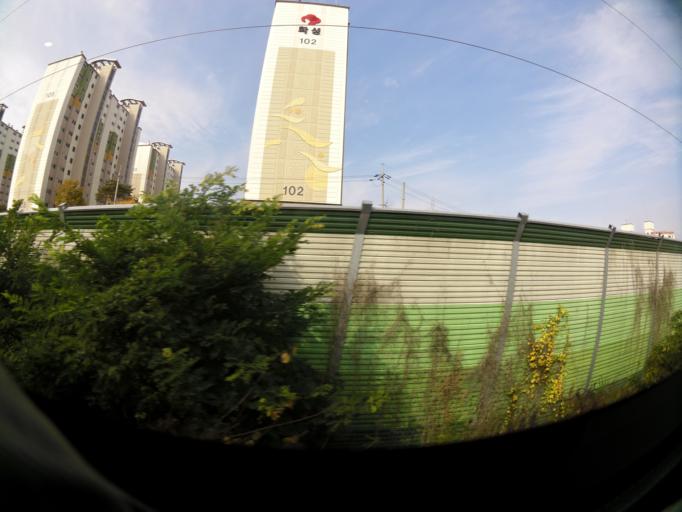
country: KR
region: Gyeongsangbuk-do
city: Gumi
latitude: 36.0984
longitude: 128.3563
